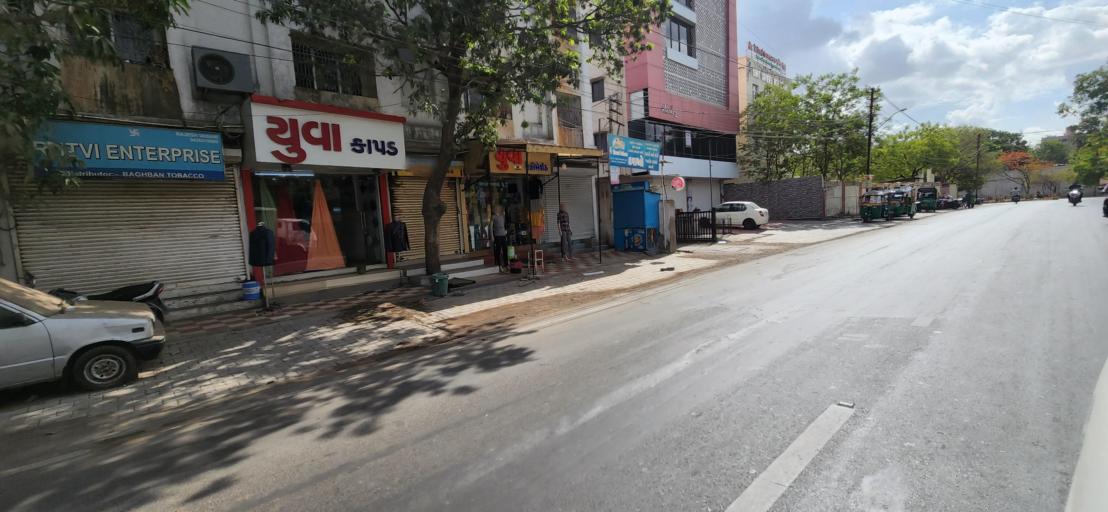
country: IN
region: Gujarat
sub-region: Bhavnagar
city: Bhavnagar
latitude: 21.7674
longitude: 72.1375
